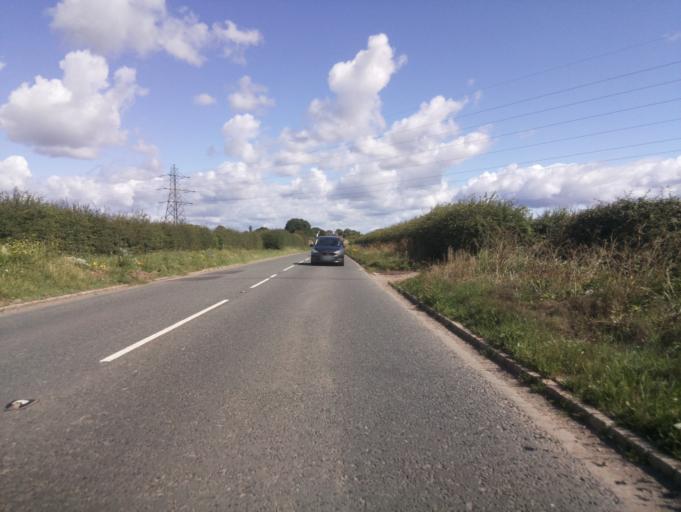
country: GB
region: England
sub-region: Gloucestershire
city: Newent
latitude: 51.9033
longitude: -2.3332
